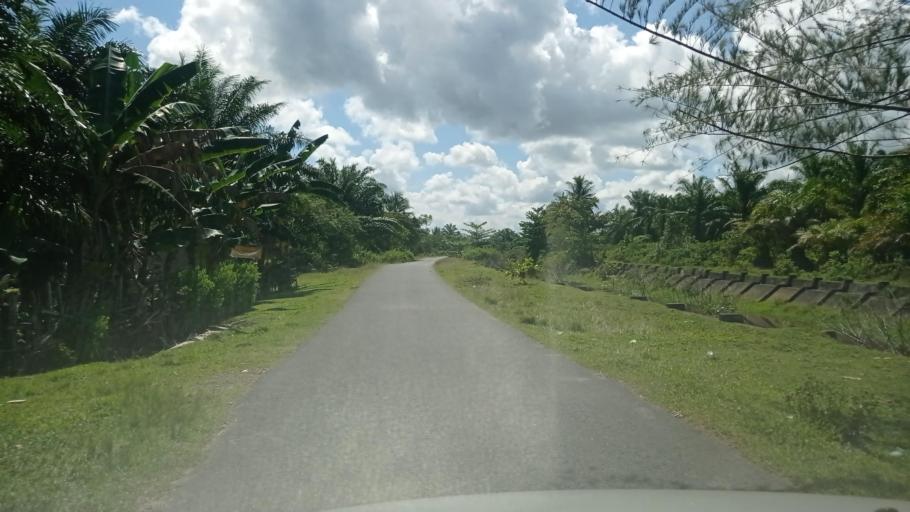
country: ID
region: Jambi
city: Sungai Penuh
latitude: -2.5521
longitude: 101.1012
